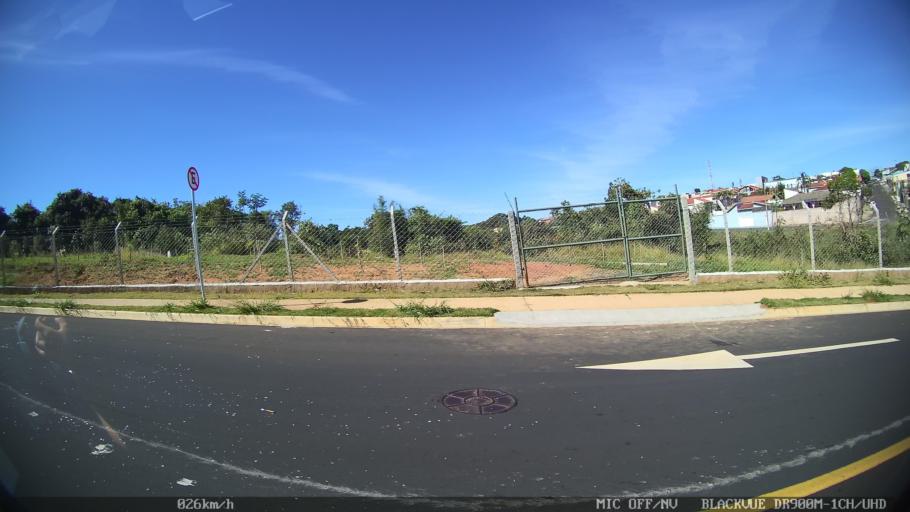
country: BR
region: Sao Paulo
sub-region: Franca
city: Franca
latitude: -20.5542
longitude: -47.3707
